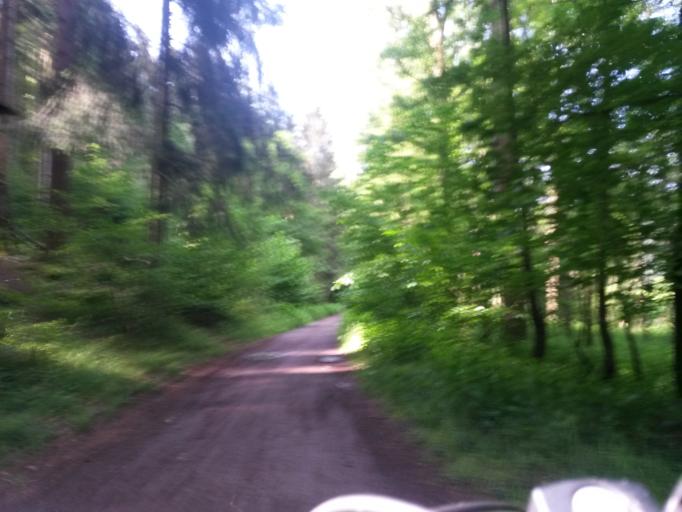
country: DE
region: Baden-Wuerttemberg
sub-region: Karlsruhe Region
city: Birkenfeld
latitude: 48.8668
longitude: 8.6466
